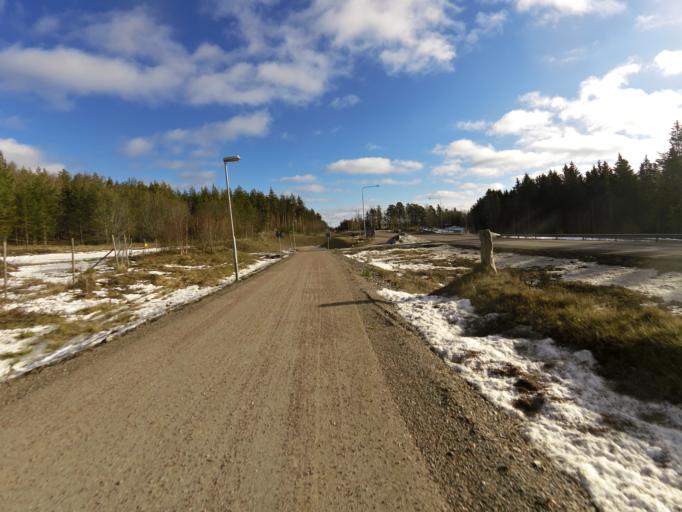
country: SE
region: Uppsala
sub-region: Alvkarleby Kommun
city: Skutskaer
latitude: 60.6501
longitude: 17.3125
